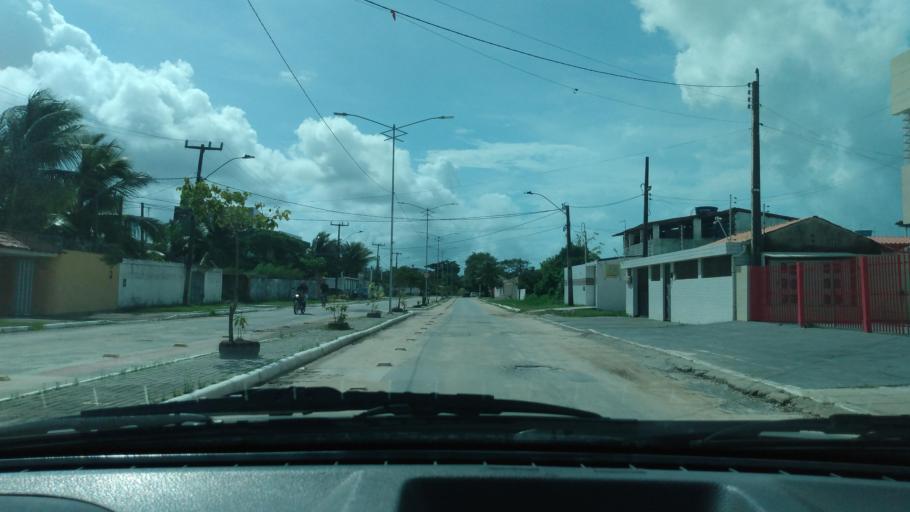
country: BR
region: Pernambuco
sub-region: Cabo De Santo Agostinho
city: Cabo
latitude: -8.3305
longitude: -34.9536
